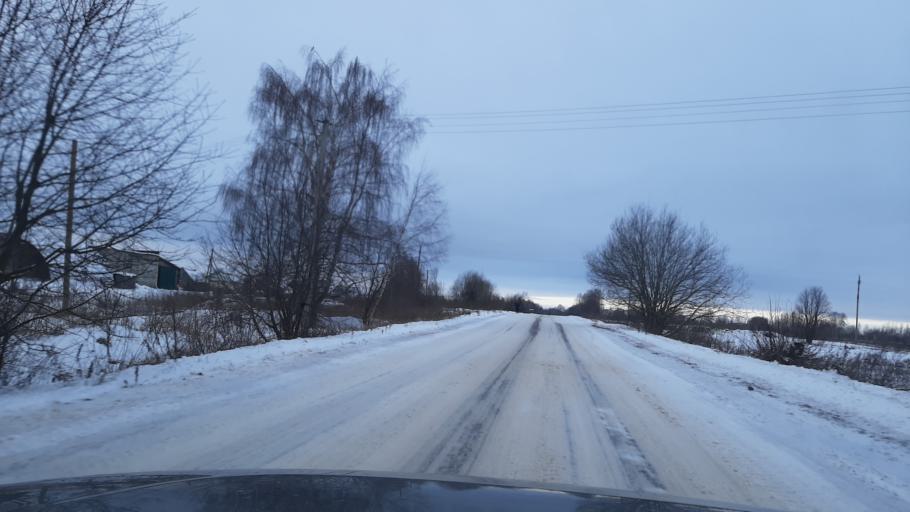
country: RU
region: Kostroma
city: Volgorechensk
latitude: 57.4351
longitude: 41.0639
